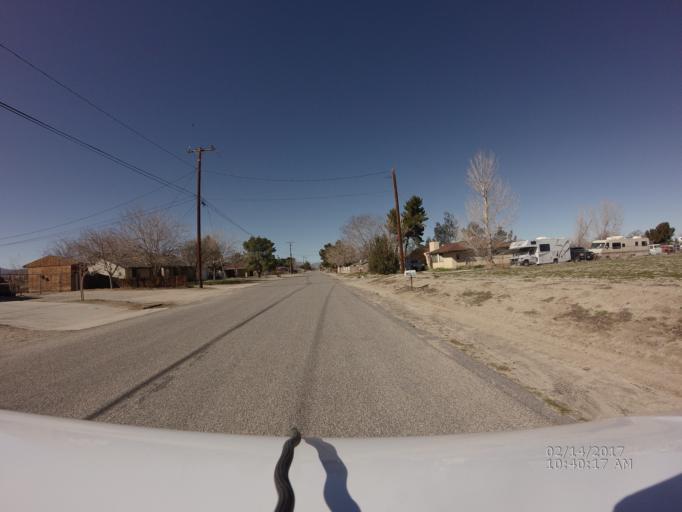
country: US
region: California
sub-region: Los Angeles County
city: Littlerock
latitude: 34.5636
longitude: -117.9358
